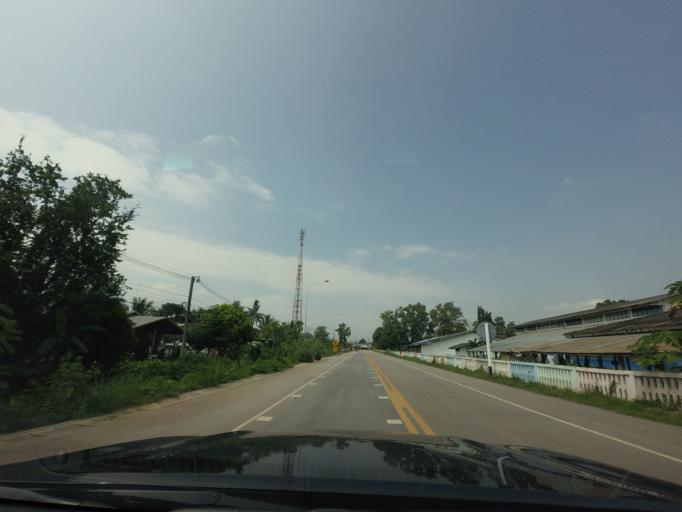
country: LA
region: Xiagnabouli
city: Muang Kenthao
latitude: 17.7045
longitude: 101.4150
